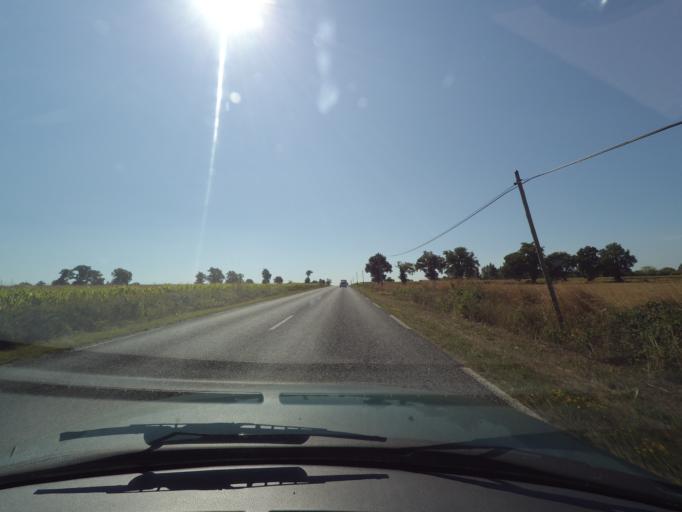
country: FR
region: Limousin
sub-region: Departement de la Haute-Vienne
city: Bellac
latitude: 46.0787
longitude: 1.0933
